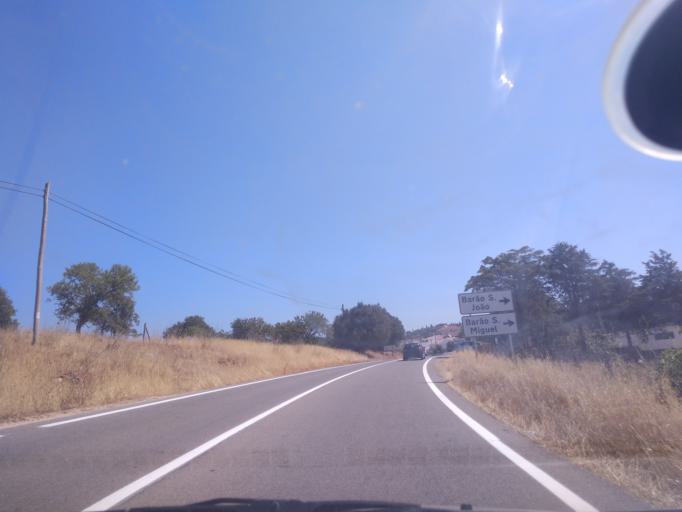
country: PT
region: Faro
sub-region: Lagos
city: Lagos
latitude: 37.1272
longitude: -8.6948
